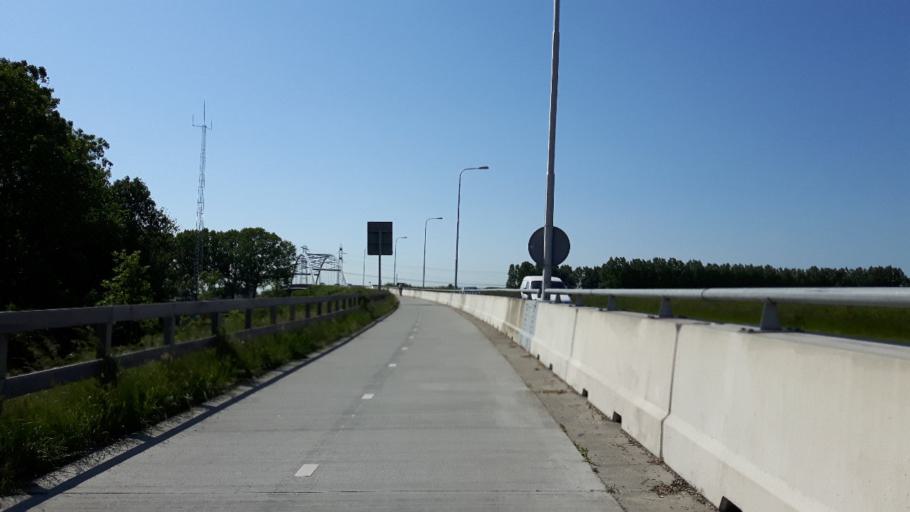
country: NL
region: Utrecht
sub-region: Stichtse Vecht
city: Vreeland
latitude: 52.2250
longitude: 5.0108
